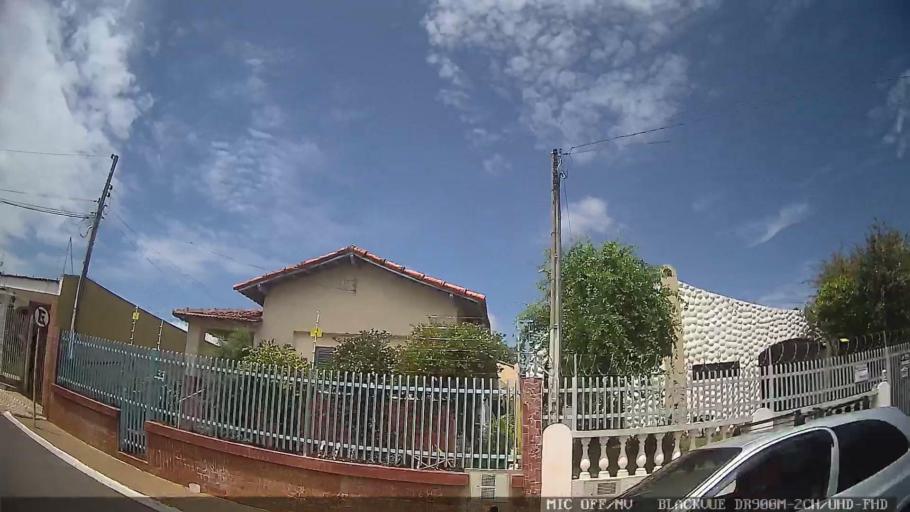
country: BR
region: Sao Paulo
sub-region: Laranjal Paulista
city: Laranjal Paulista
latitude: -23.0558
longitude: -47.8353
